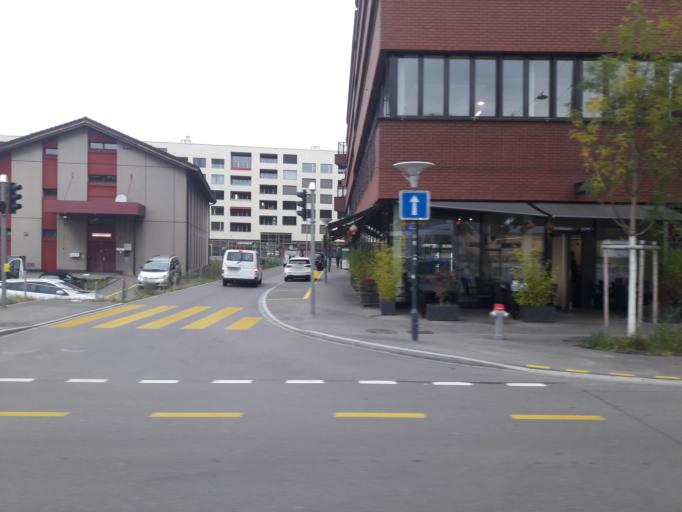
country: CH
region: Zurich
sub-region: Bezirk Dietikon
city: Schlieren / Zentrum
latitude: 47.3981
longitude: 8.4468
